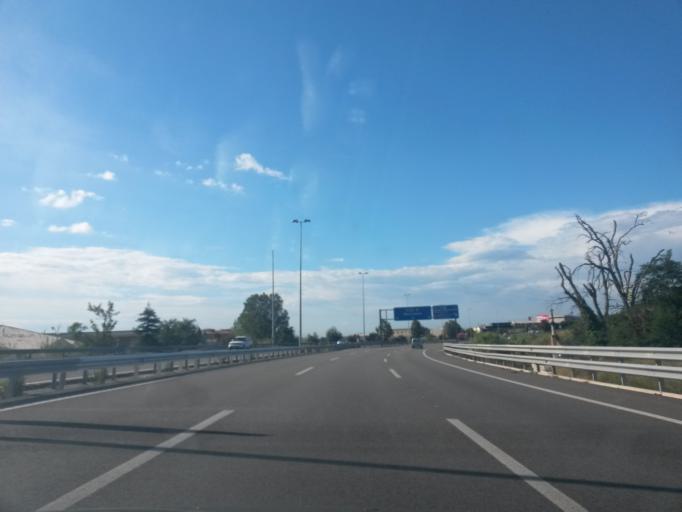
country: ES
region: Catalonia
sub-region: Provincia de Barcelona
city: Argentona
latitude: 41.5359
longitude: 2.4171
